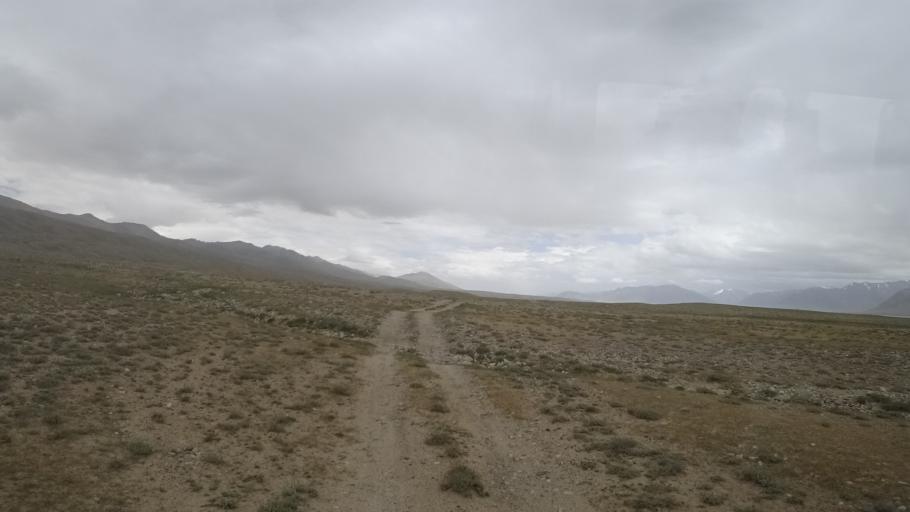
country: TJ
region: Gorno-Badakhshan
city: Murghob
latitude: 37.4756
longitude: 73.7020
